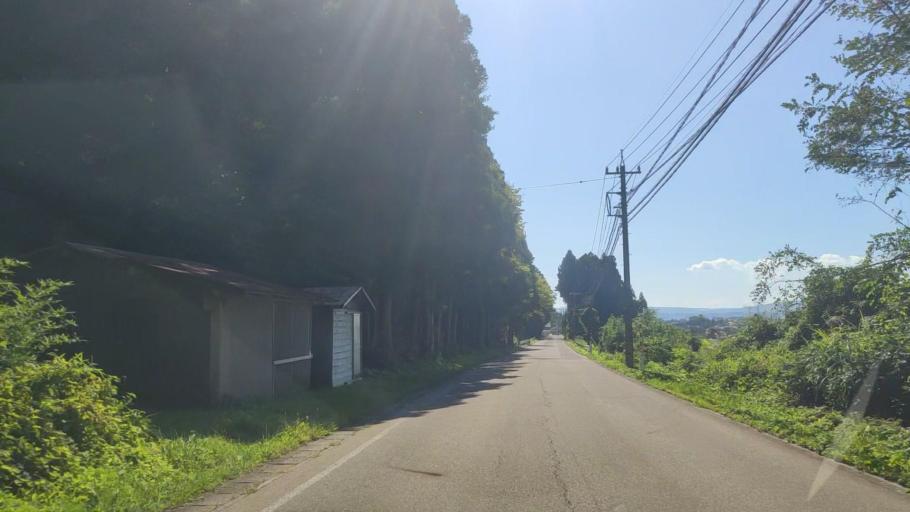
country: JP
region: Ishikawa
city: Nanao
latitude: 37.4537
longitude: 137.3009
